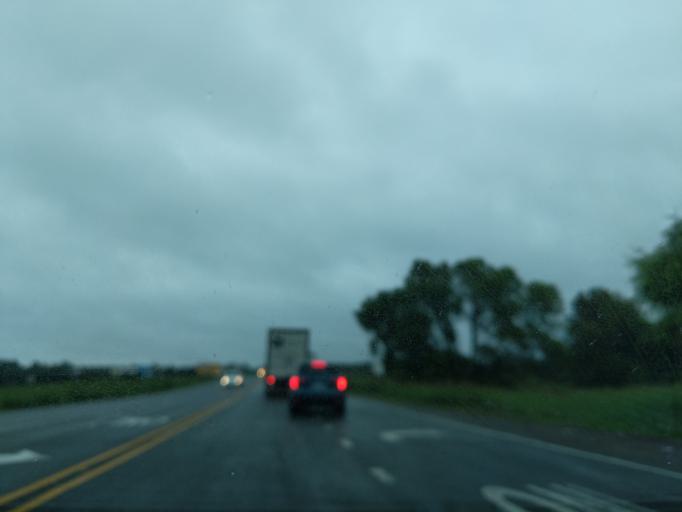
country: US
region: Louisiana
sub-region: Caddo Parish
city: Greenwood
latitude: 32.4439
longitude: -93.9814
